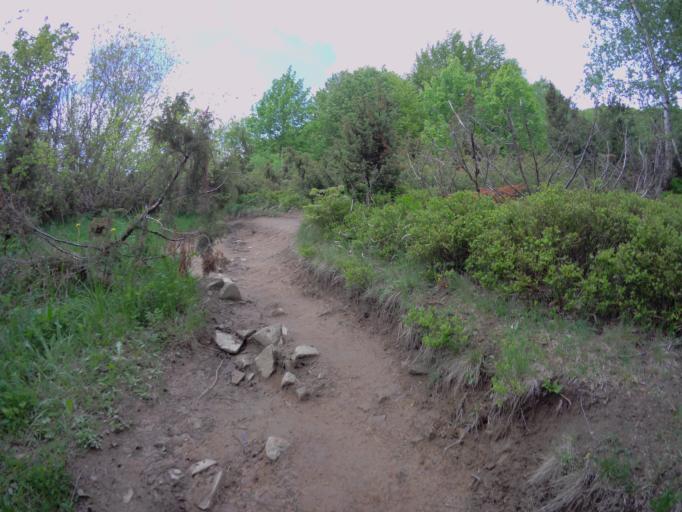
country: PL
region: Subcarpathian Voivodeship
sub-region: Powiat bieszczadzki
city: Lutowiska
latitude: 49.1482
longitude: 22.5597
